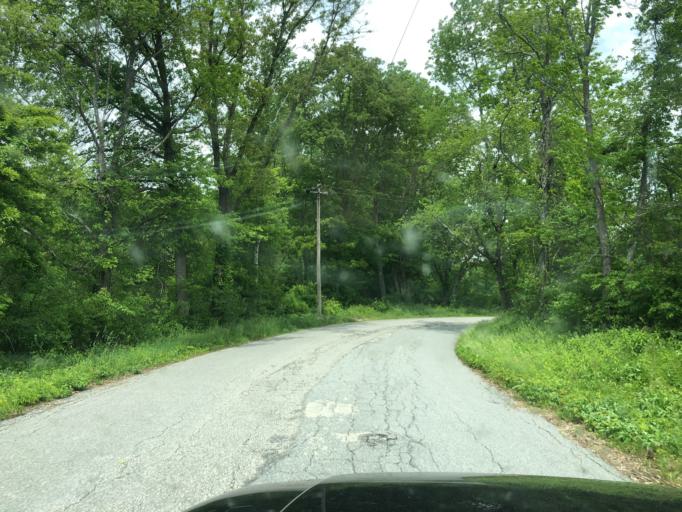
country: US
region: Connecticut
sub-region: Windham County
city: Thompson
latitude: 41.9671
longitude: -71.8431
